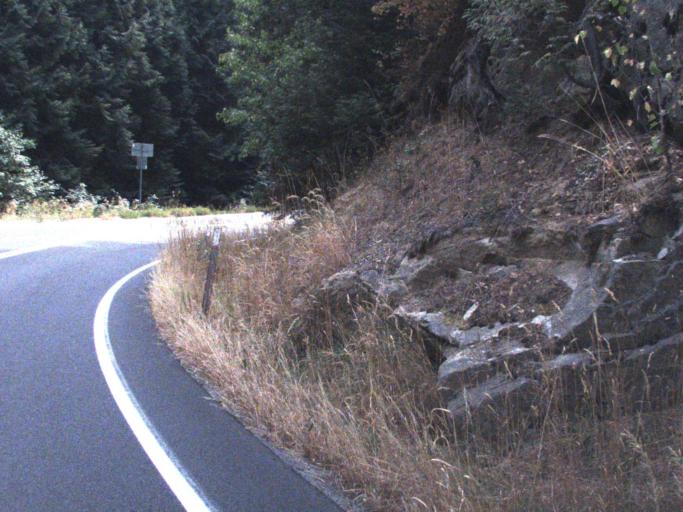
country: US
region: Washington
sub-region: Spokane County
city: Otis Orchards-East Farms
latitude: 47.8767
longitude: -117.1487
